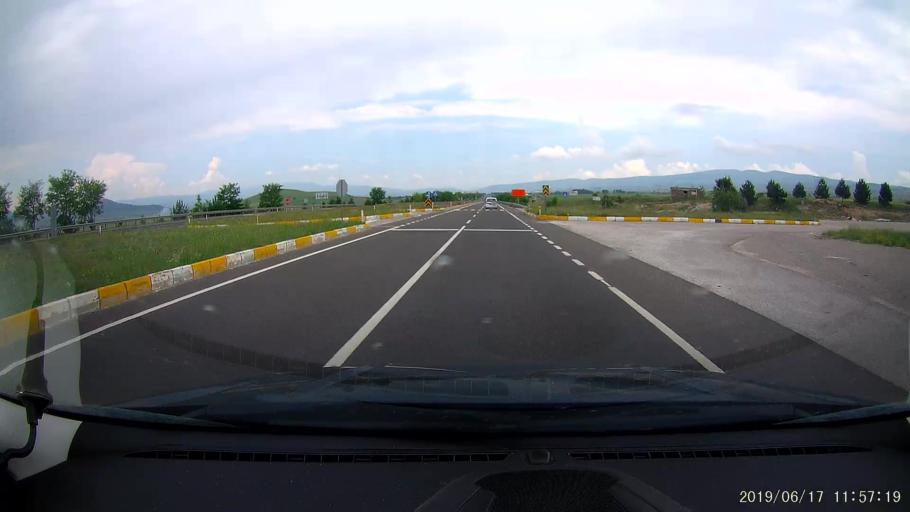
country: TR
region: Cankiri
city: Cerkes
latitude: 40.8070
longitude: 32.9613
